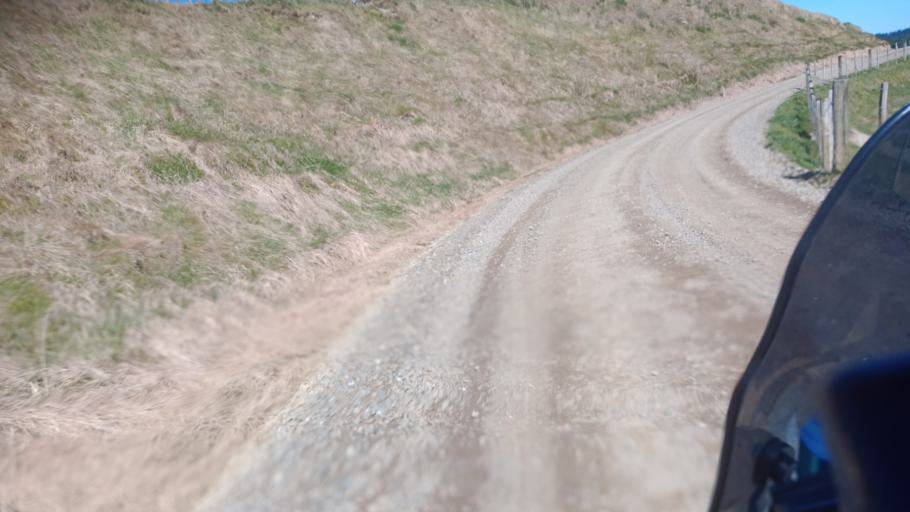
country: NZ
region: Gisborne
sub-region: Gisborne District
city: Gisborne
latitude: -39.1699
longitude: 177.8997
